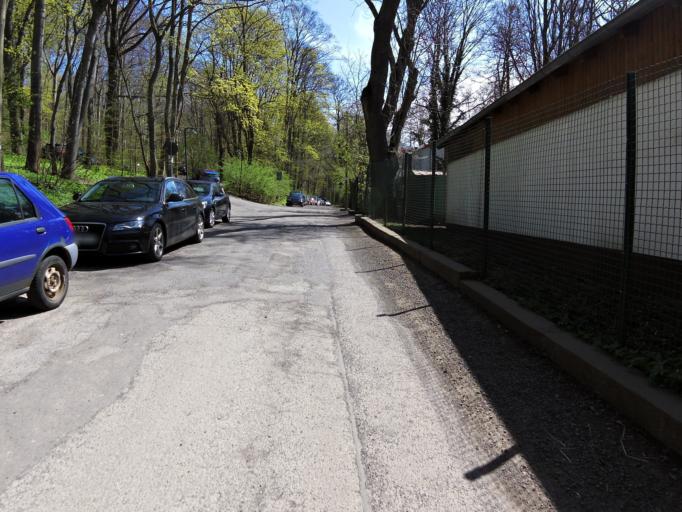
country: DE
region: Thuringia
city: Gotha
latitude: 50.9353
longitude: 10.7196
